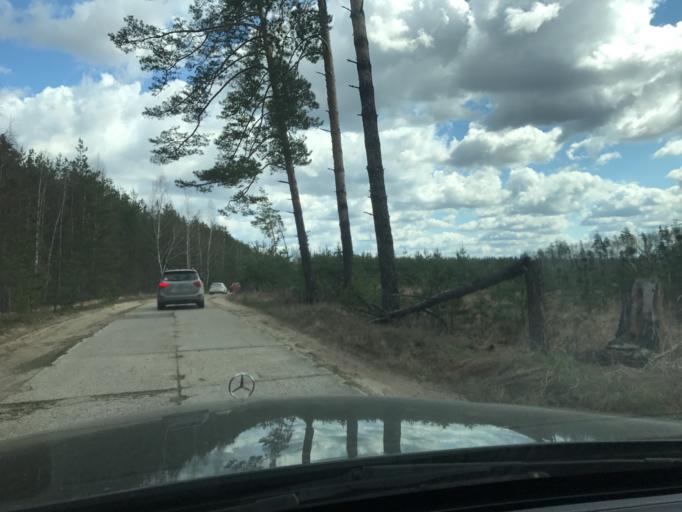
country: RU
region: Vladimir
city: Pokrov
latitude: 55.8460
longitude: 39.1526
